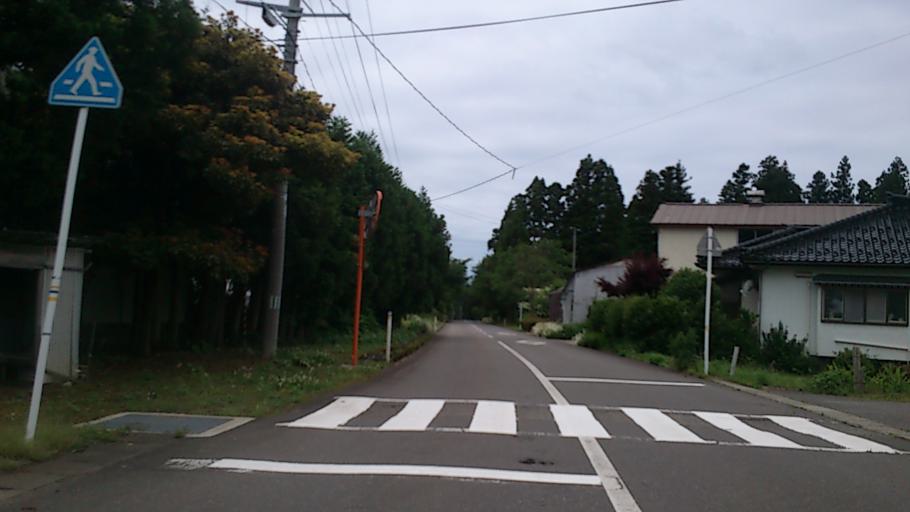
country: JP
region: Yamagata
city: Yuza
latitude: 39.0862
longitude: 139.9021
